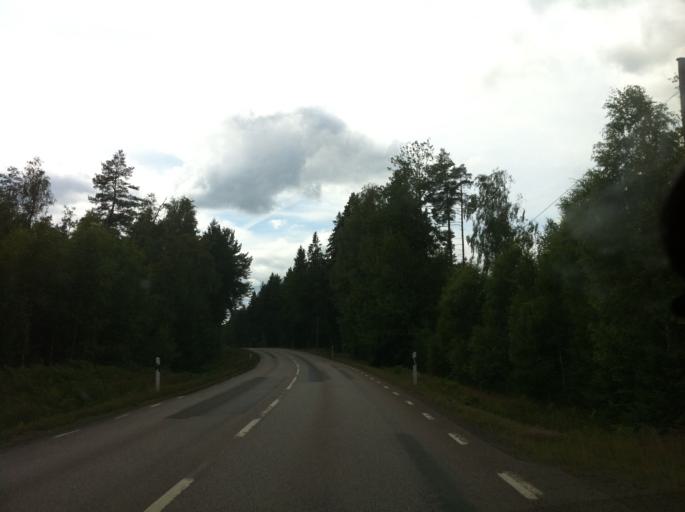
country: SE
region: Kalmar
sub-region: Emmaboda Kommun
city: Emmaboda
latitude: 56.6372
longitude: 15.6651
